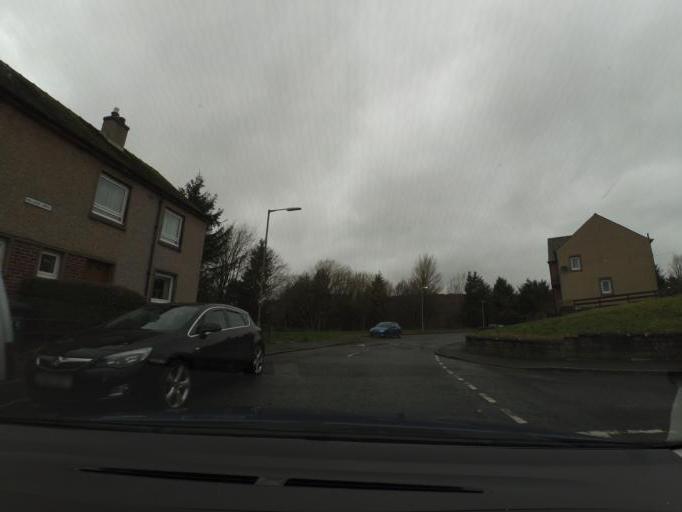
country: GB
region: Scotland
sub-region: The Scottish Borders
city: Hawick
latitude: 55.4350
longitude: -2.7776
